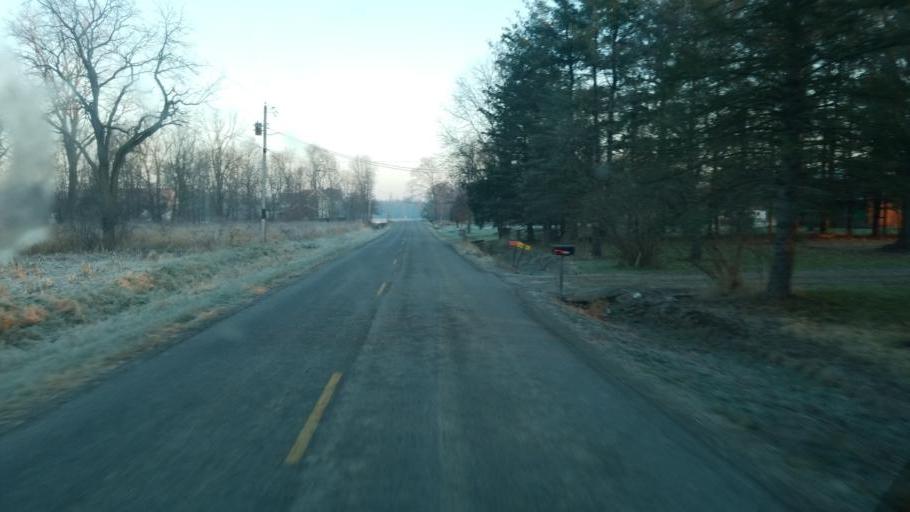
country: US
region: Ohio
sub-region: Medina County
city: Lodi
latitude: 40.9975
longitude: -82.0360
